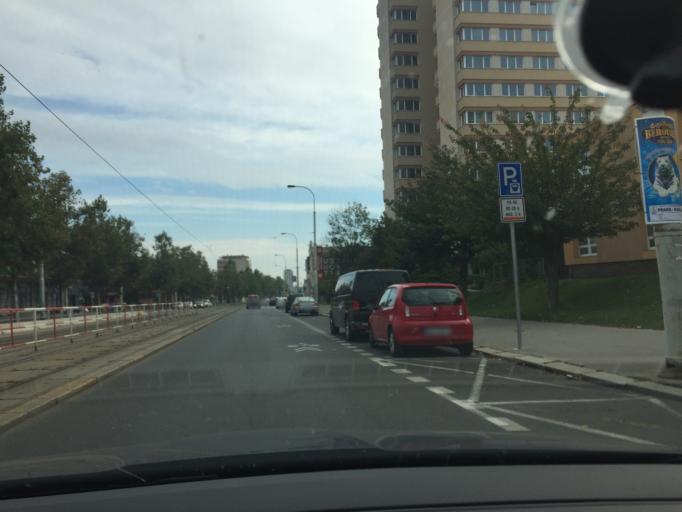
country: CZ
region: Praha
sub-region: Praha 8
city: Liben
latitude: 50.0925
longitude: 14.4869
